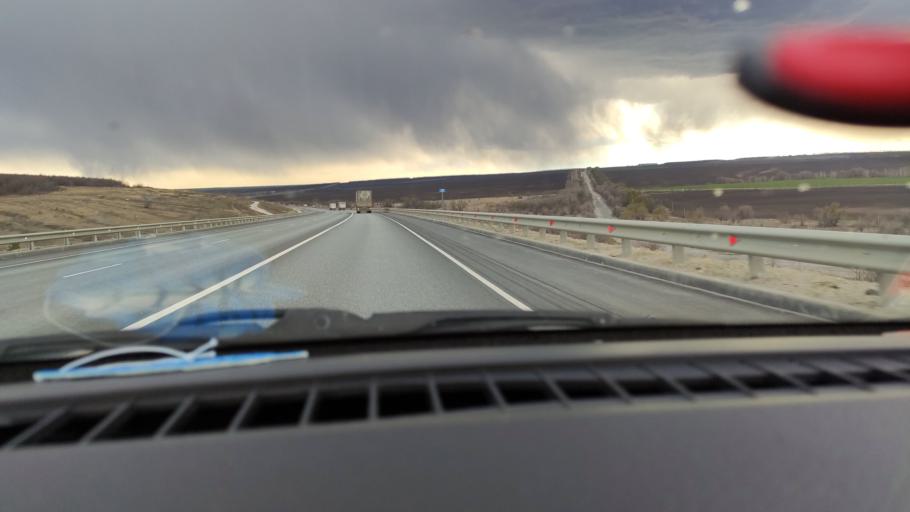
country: RU
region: Saratov
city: Yelshanka
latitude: 51.8763
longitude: 46.5068
